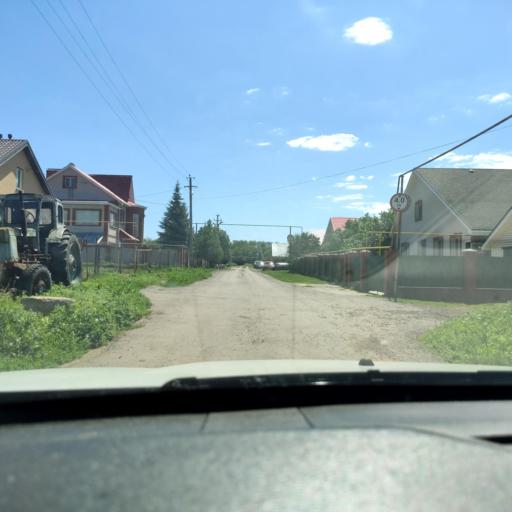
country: RU
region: Samara
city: Dubovyy Umet
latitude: 53.0344
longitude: 50.2486
